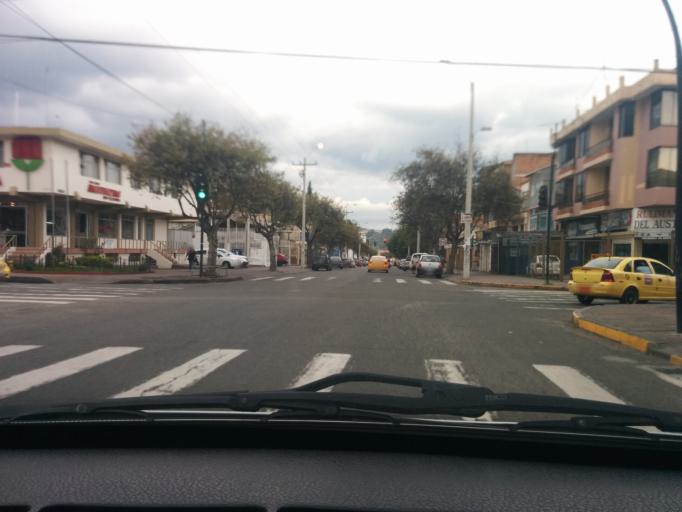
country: EC
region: Azuay
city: Cuenca
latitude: -2.8983
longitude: -78.9941
